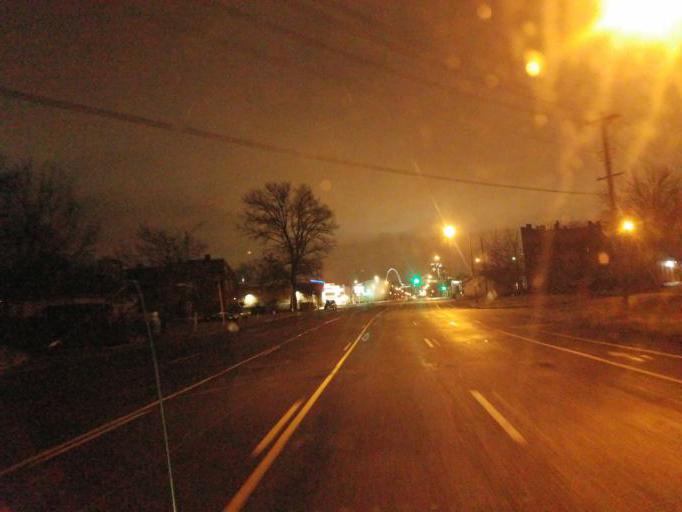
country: US
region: Missouri
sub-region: City of Saint Louis
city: St. Louis
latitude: 38.6518
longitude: -90.2008
